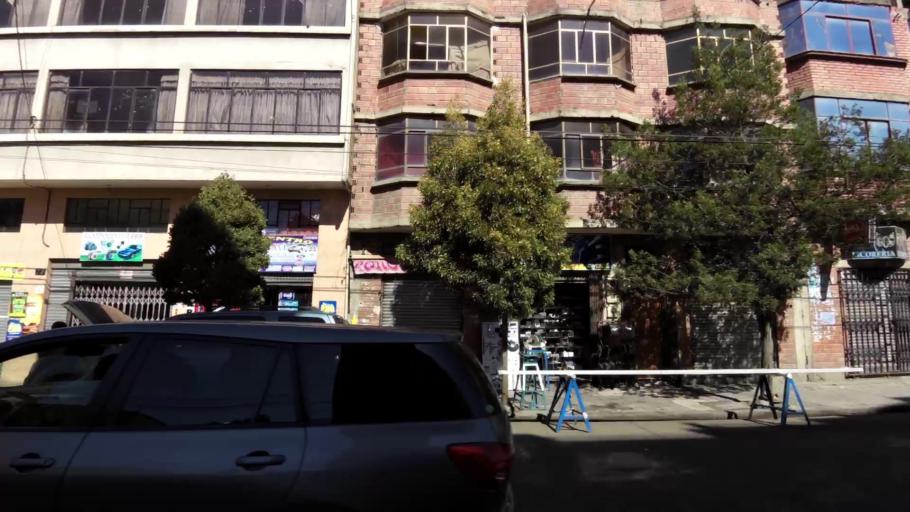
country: BO
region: La Paz
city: La Paz
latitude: -16.5144
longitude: -68.1562
